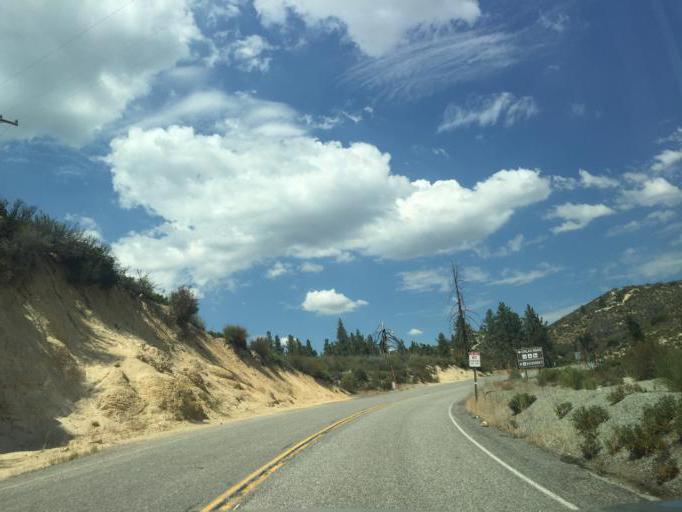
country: US
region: California
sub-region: Los Angeles County
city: Sierra Madre
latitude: 34.3176
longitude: -118.0106
